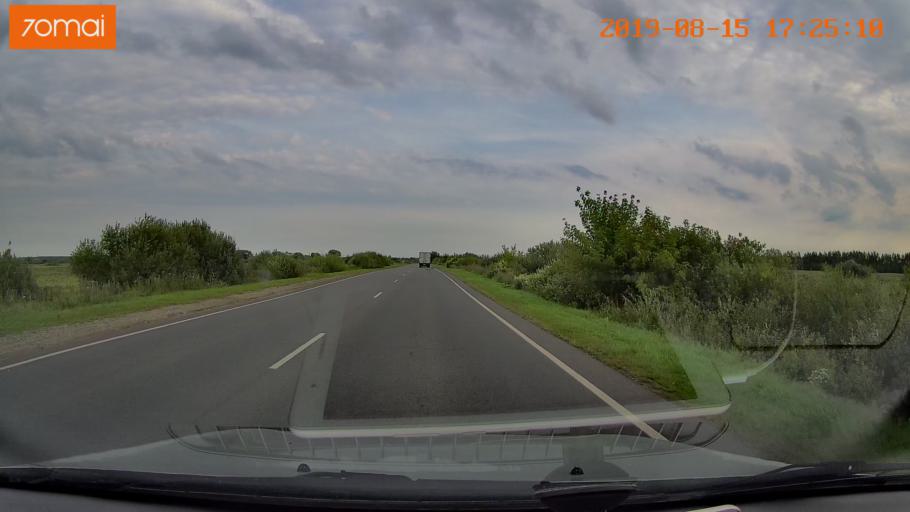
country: RU
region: Moskovskaya
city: Ashitkovo
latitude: 55.3781
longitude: 38.5625
